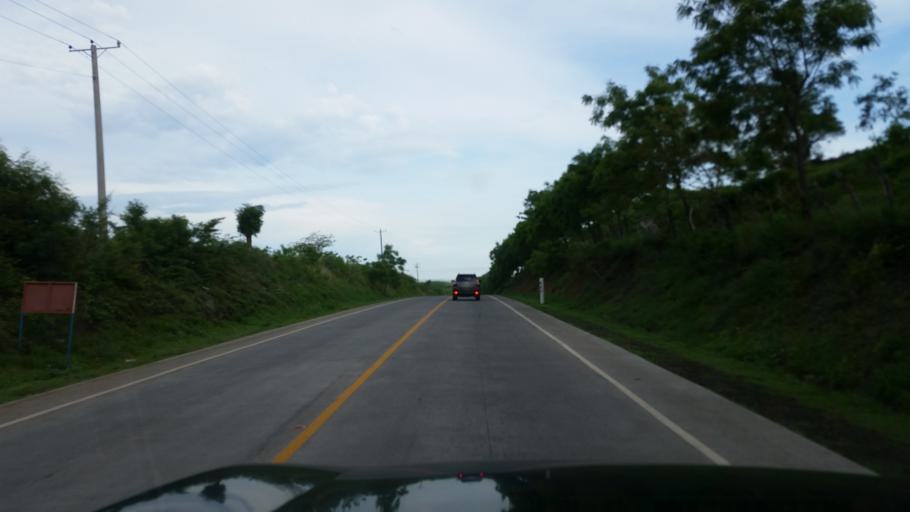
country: NI
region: Managua
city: Carlos Fonseca Amador
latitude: 12.0738
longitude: -86.4970
